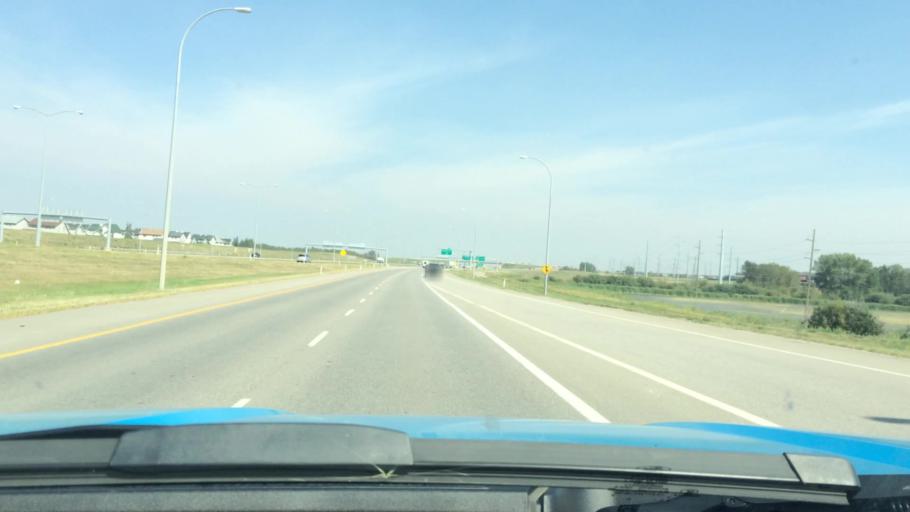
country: CA
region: Alberta
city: Okotoks
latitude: 50.9012
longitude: -113.9658
